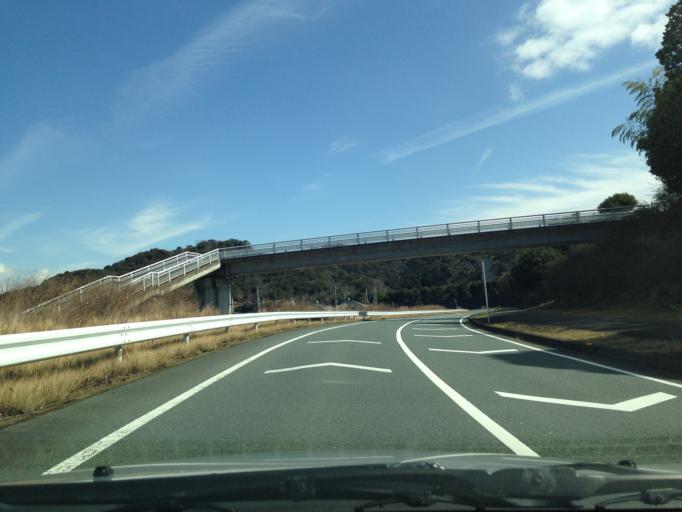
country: JP
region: Shizuoka
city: Fukuroi
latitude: 34.7468
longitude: 137.9678
